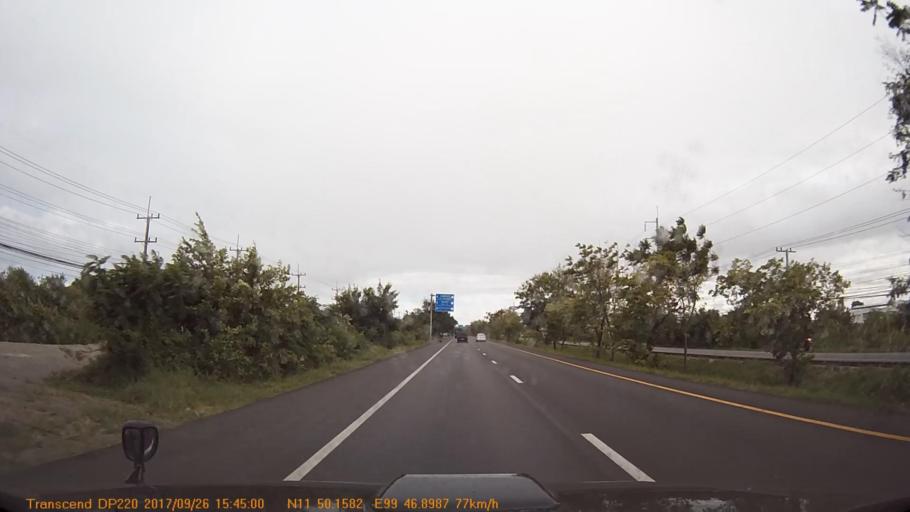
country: TH
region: Prachuap Khiri Khan
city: Prachuap Khiri Khan
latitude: 11.8359
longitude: 99.7816
